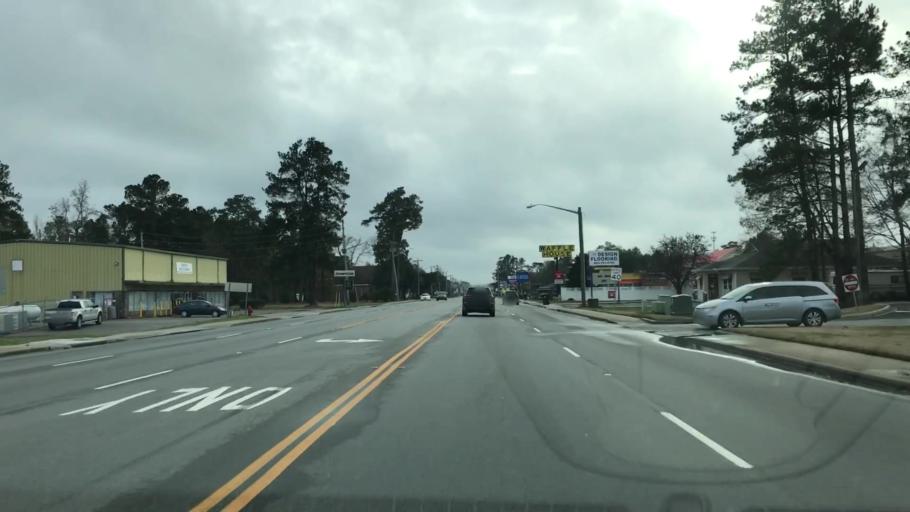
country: US
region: South Carolina
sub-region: Berkeley County
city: Moncks Corner
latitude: 33.1998
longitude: -79.9915
